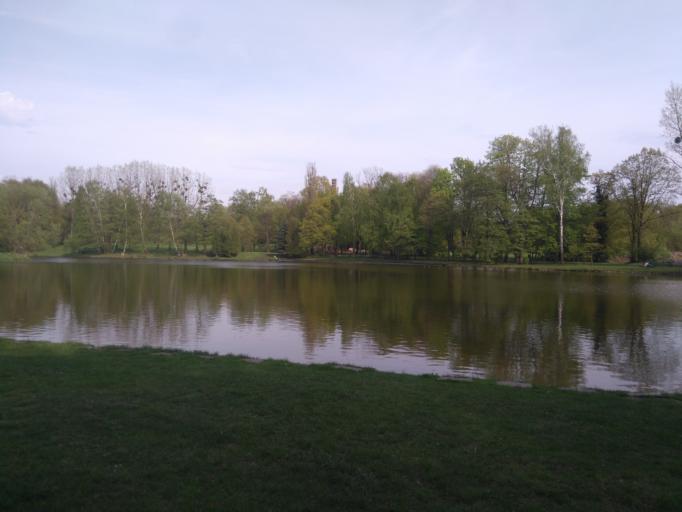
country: PL
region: Lodz Voivodeship
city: Lodz
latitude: 51.7669
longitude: 19.4107
